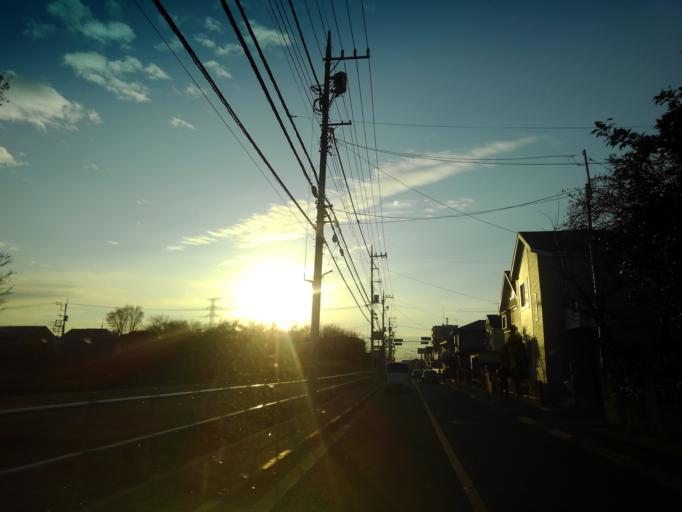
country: JP
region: Tokyo
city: Kokubunji
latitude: 35.7057
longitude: 139.4519
